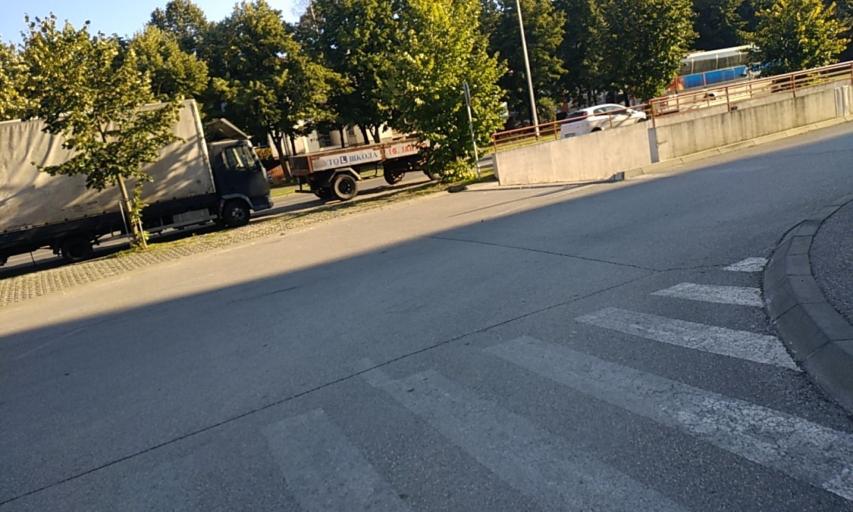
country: BA
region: Republika Srpska
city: Starcevica
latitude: 44.7635
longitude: 17.2048
